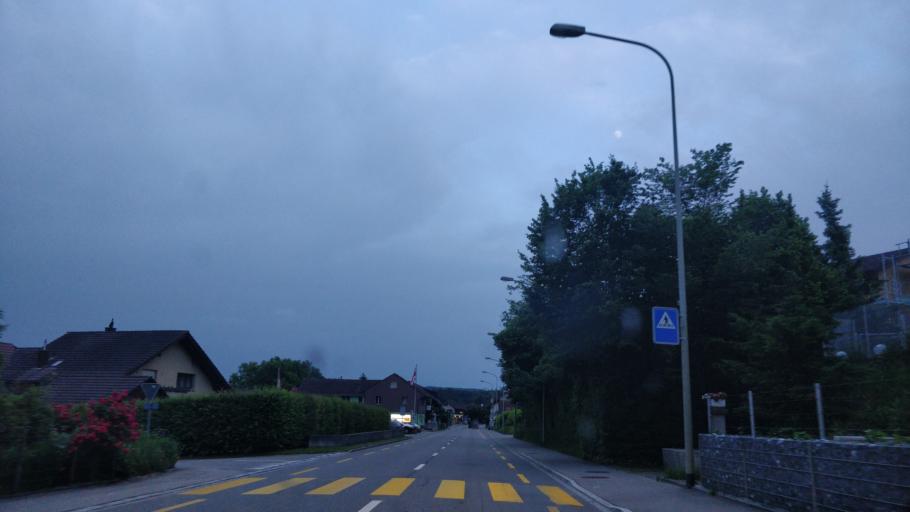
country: CH
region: Zurich
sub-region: Bezirk Buelach
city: Rorbas
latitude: 47.5337
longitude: 8.5710
